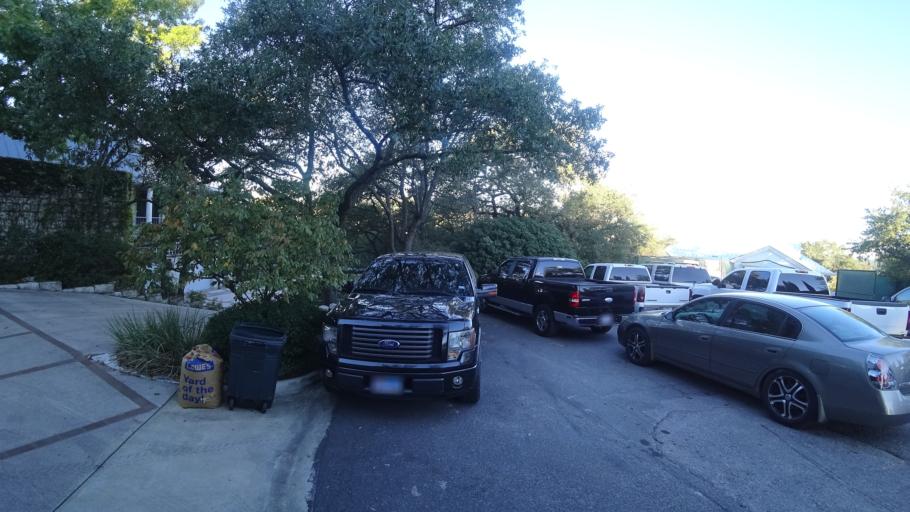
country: US
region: Texas
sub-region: Travis County
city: West Lake Hills
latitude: 30.3049
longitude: -97.7759
